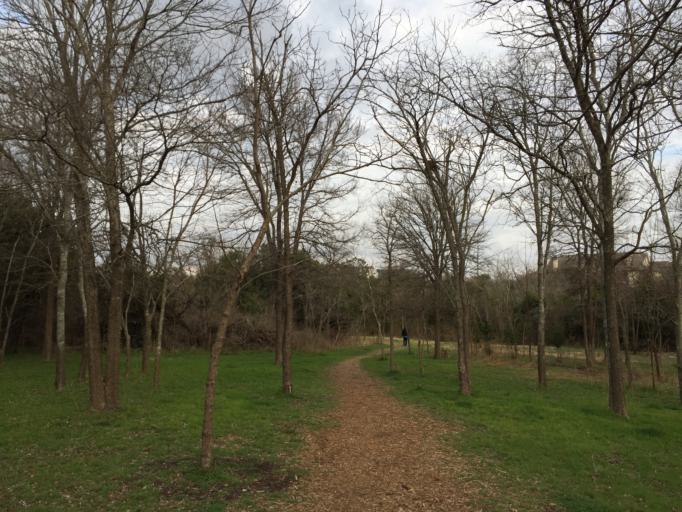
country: US
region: Texas
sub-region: Travis County
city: Wells Branch
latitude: 30.3898
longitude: -97.6781
